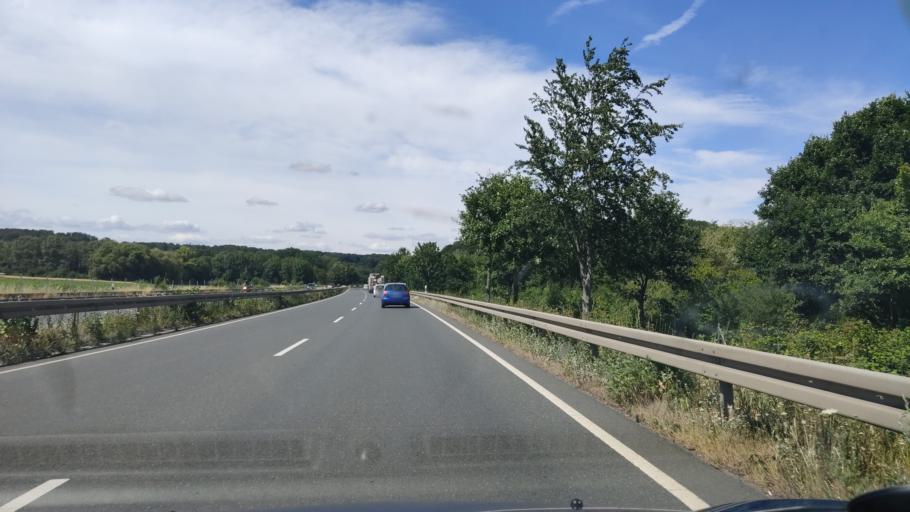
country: DE
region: Lower Saxony
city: Ronnenberg
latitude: 52.3398
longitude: 9.6438
